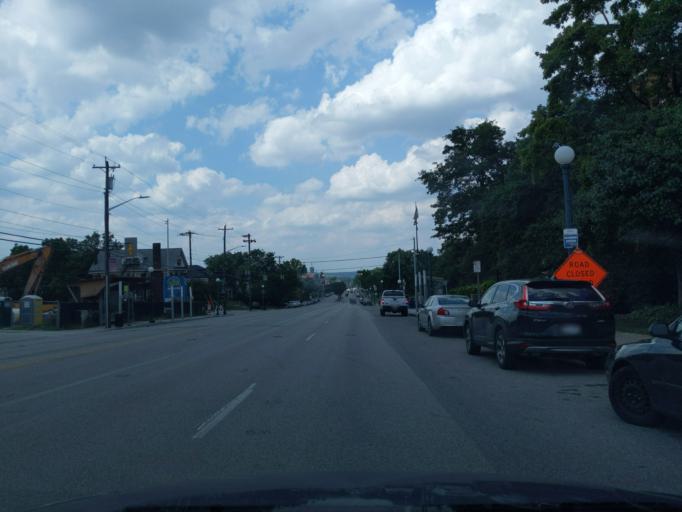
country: US
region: Ohio
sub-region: Hamilton County
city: Saint Bernard
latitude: 39.1289
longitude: -84.5207
